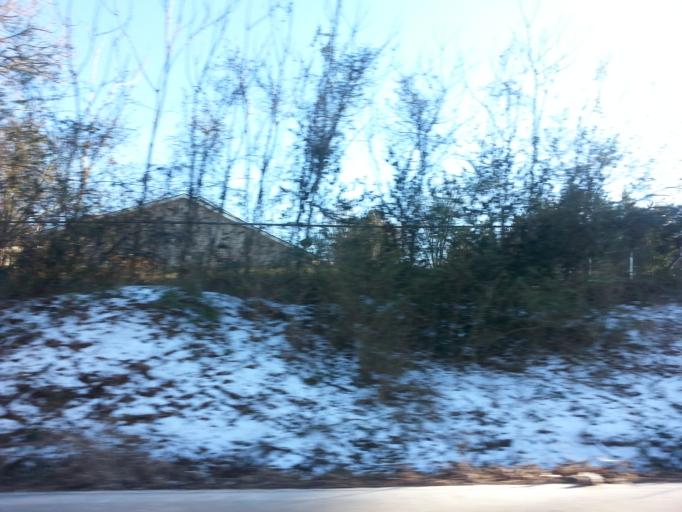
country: US
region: Tennessee
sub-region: Knox County
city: Farragut
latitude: 35.9561
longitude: -84.0557
